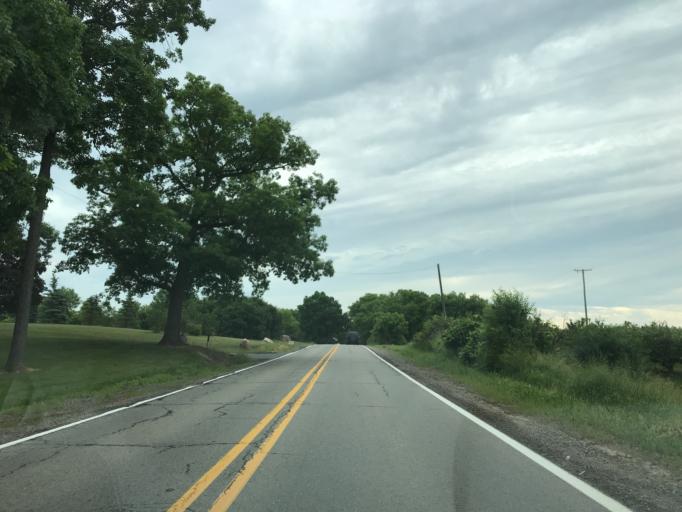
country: US
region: Michigan
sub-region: Oakland County
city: South Lyon
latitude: 42.5036
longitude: -83.6646
